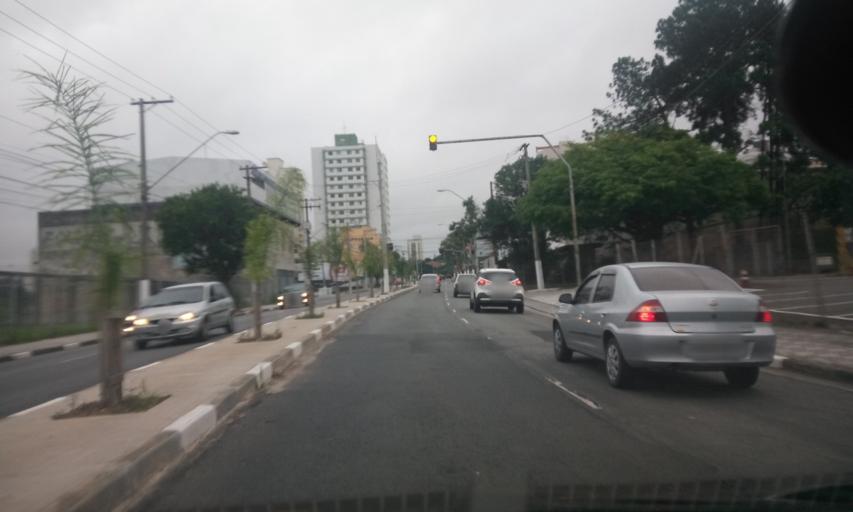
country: BR
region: Sao Paulo
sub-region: Sao Bernardo Do Campo
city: Sao Bernardo do Campo
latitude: -23.6802
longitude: -46.5553
